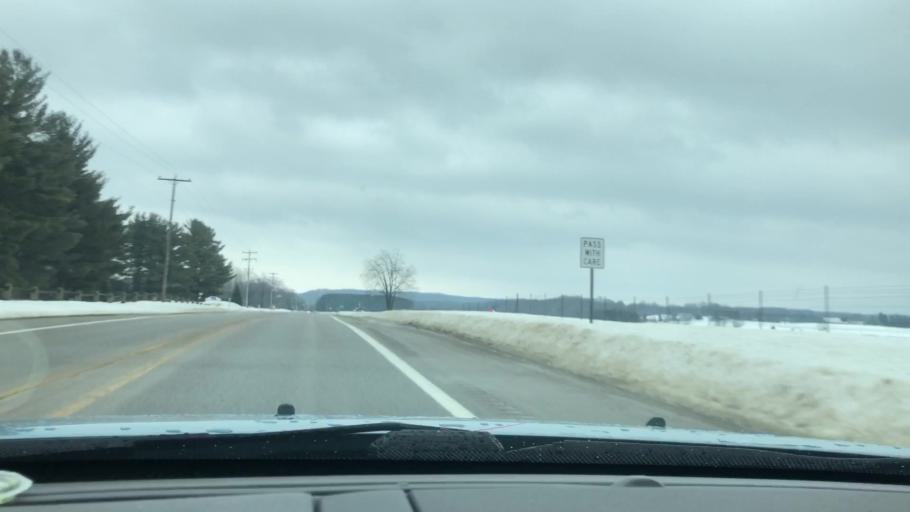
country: US
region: Michigan
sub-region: Charlevoix County
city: East Jordan
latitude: 45.1325
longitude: -85.1116
